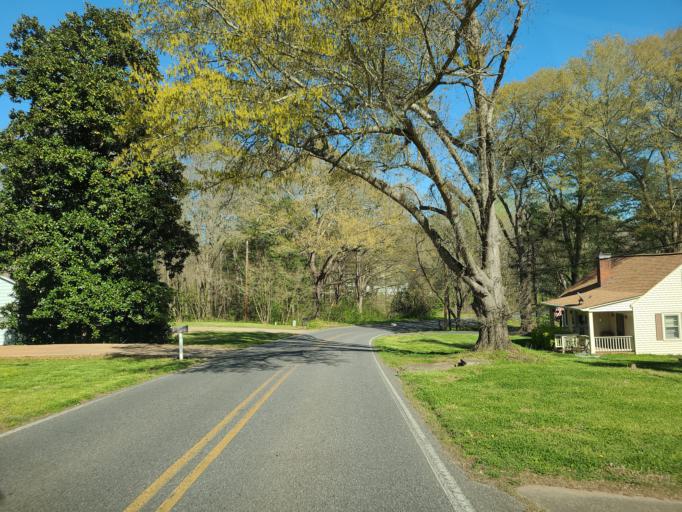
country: US
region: North Carolina
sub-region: Cleveland County
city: Shelby
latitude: 35.2737
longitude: -81.5613
